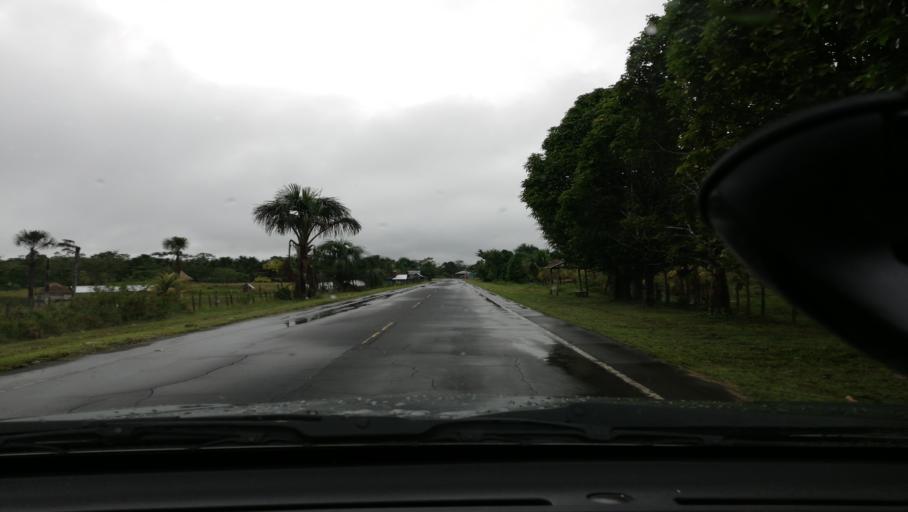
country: PE
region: Loreto
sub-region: Provincia de Maynas
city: San Juan
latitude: -4.1065
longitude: -73.4570
